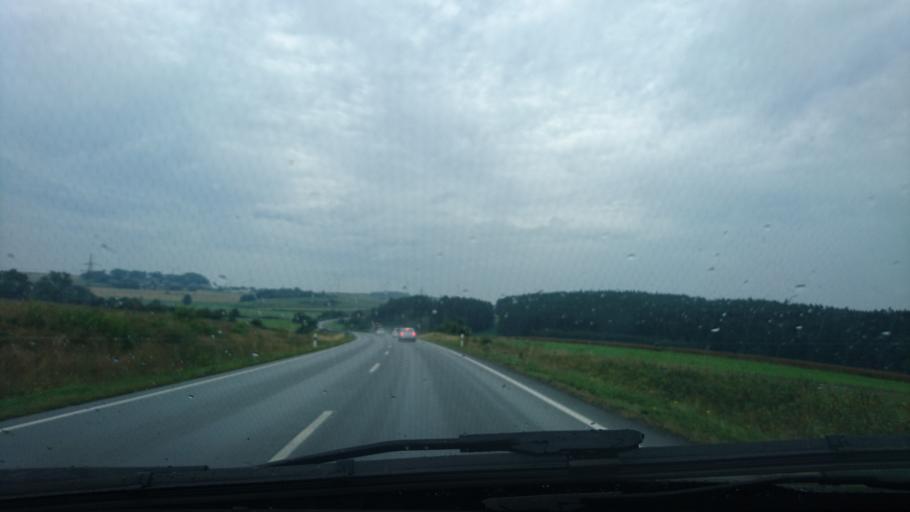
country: DE
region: Bavaria
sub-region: Upper Franconia
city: Selbitz
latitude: 50.3281
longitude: 11.7503
